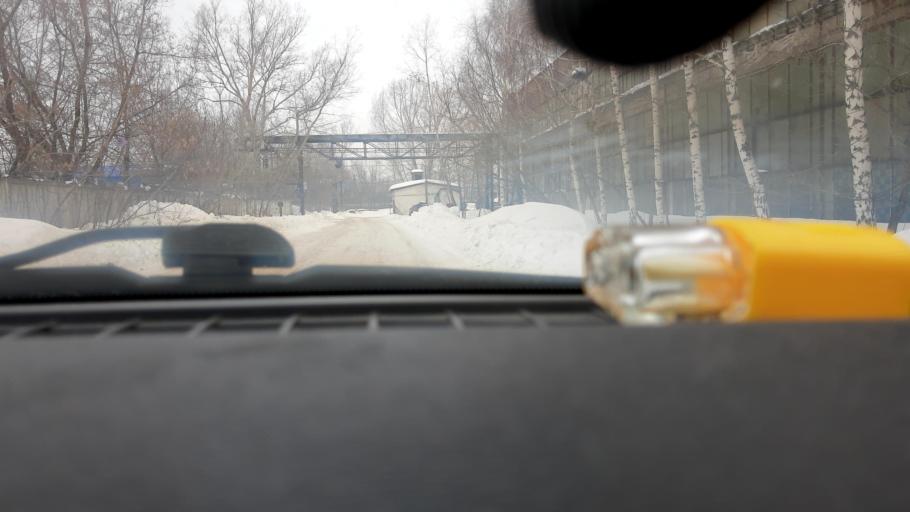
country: RU
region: Bashkortostan
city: Ufa
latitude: 54.8331
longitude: 56.1106
